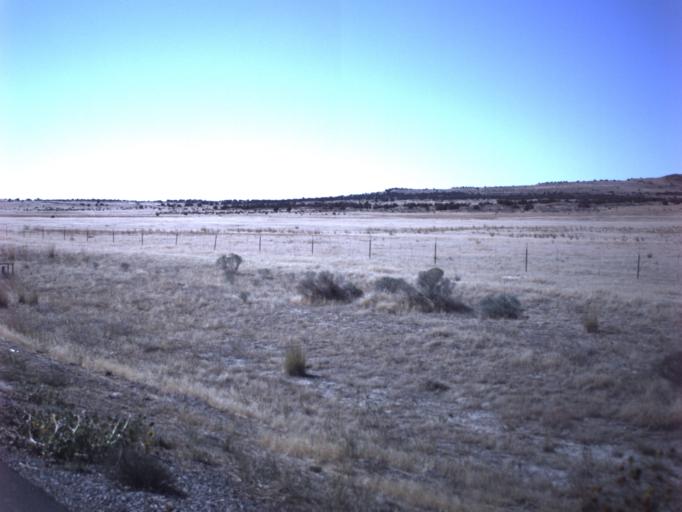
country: US
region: Utah
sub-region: Tooele County
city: Grantsville
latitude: 40.2608
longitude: -112.7407
